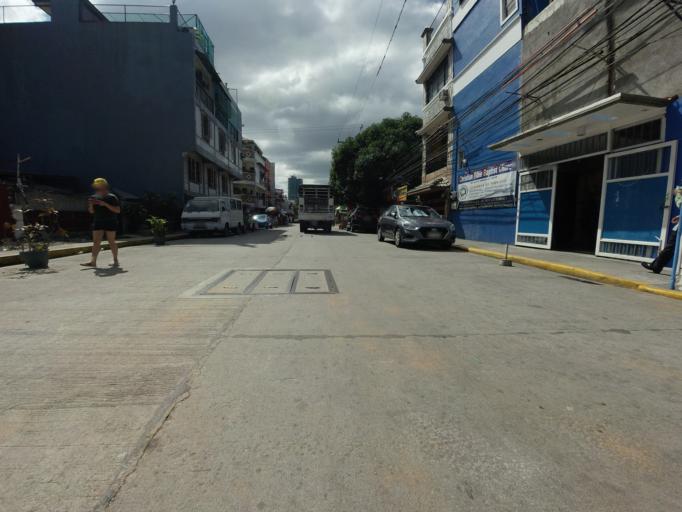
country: PH
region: Metro Manila
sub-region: City of Manila
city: Quiapo
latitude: 14.5712
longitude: 121.0036
